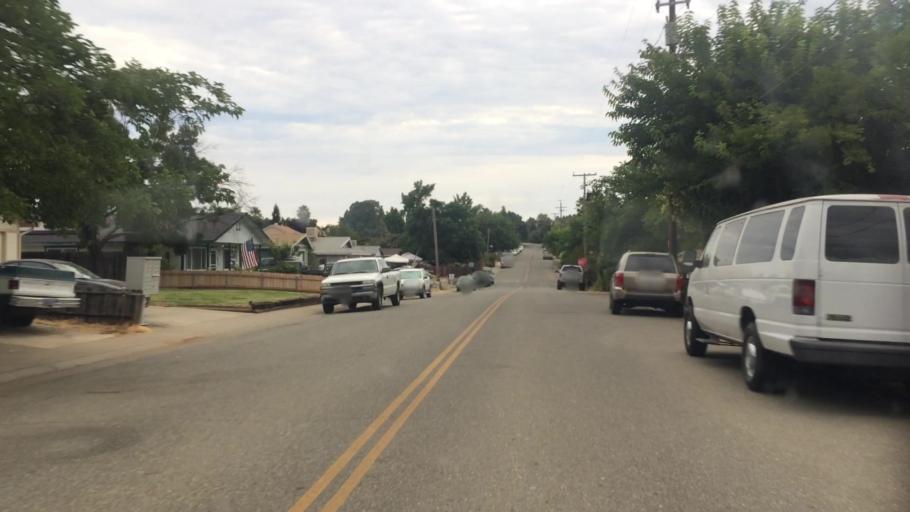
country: US
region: California
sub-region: Amador County
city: Ione
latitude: 38.3556
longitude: -120.9411
